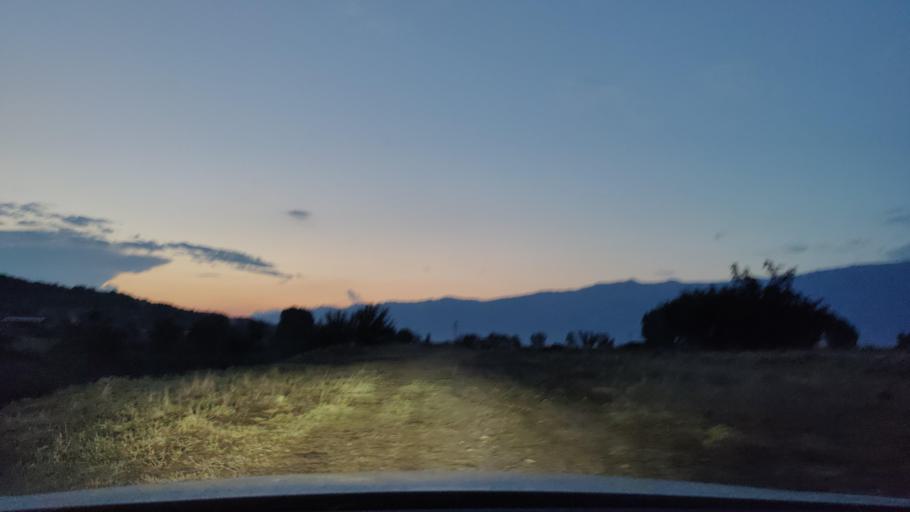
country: GR
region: Central Macedonia
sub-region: Nomos Serron
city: Chrysochorafa
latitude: 41.2044
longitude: 23.0778
